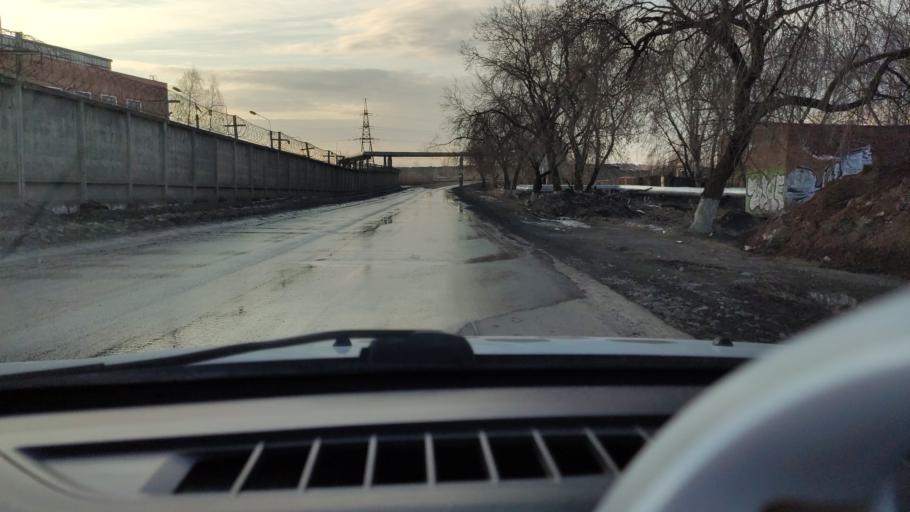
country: RU
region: Perm
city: Perm
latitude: 58.0392
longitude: 56.3083
